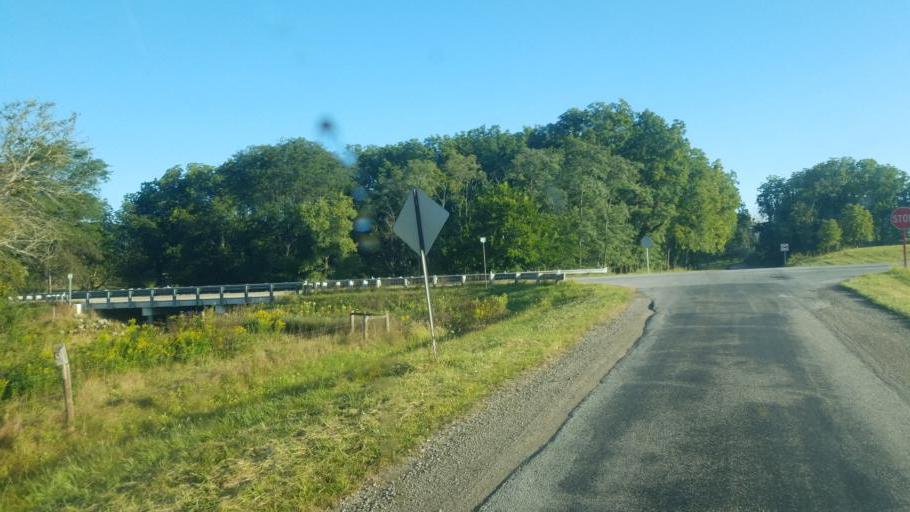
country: US
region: Ohio
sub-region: Lorain County
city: Wellington
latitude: 41.1023
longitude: -82.2789
